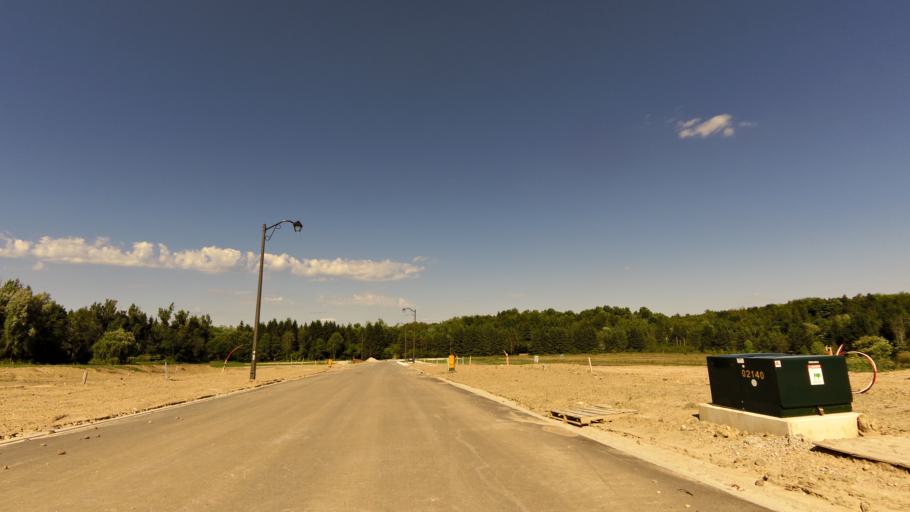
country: CA
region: Ontario
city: Brampton
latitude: 43.7601
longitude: -79.9254
